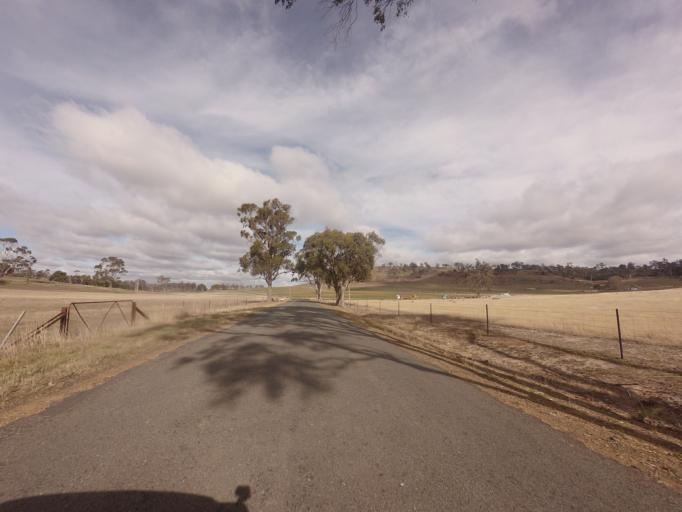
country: AU
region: Tasmania
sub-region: Brighton
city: Bridgewater
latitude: -42.3897
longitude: 147.3648
